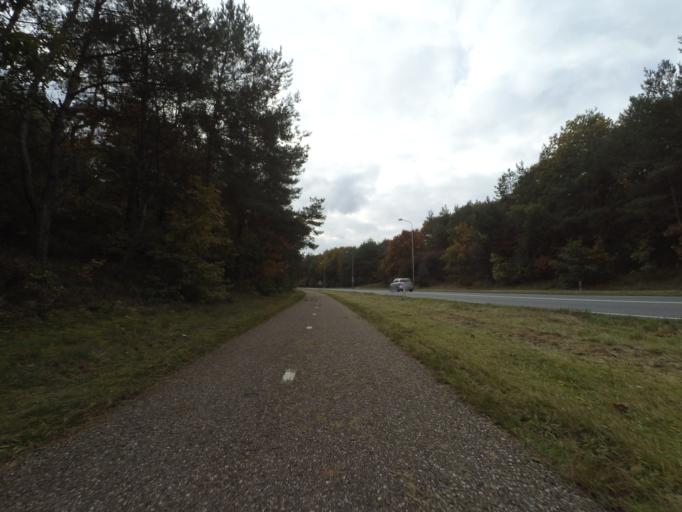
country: NL
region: Gelderland
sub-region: Gemeente Ermelo
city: Ermelo
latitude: 52.3026
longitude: 5.6795
